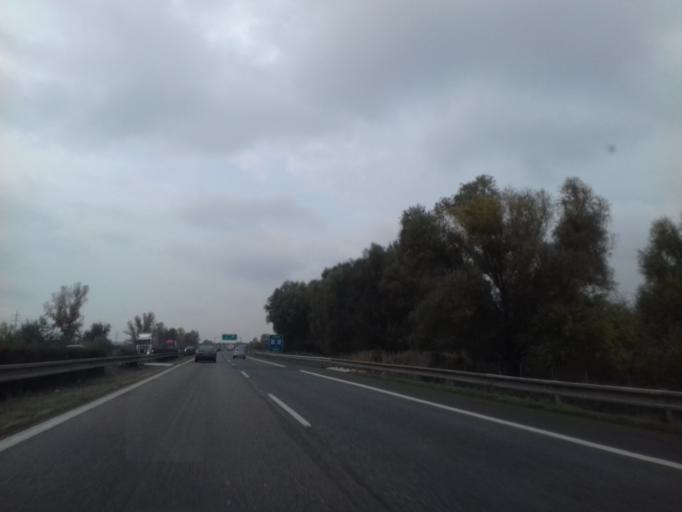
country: SK
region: Bratislavsky
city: Stupava
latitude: 48.2379
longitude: 17.0178
